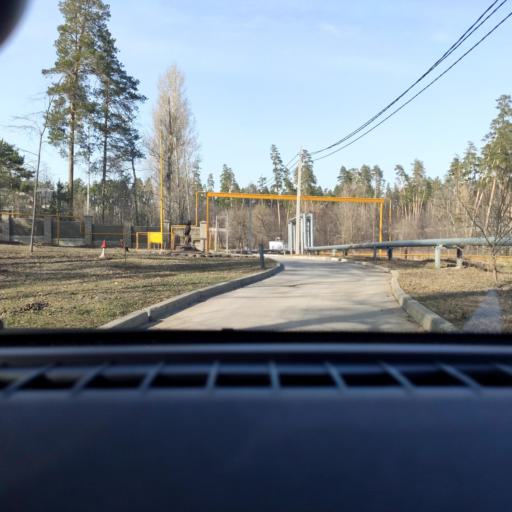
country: RU
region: Samara
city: Tol'yatti
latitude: 53.4994
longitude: 49.3585
